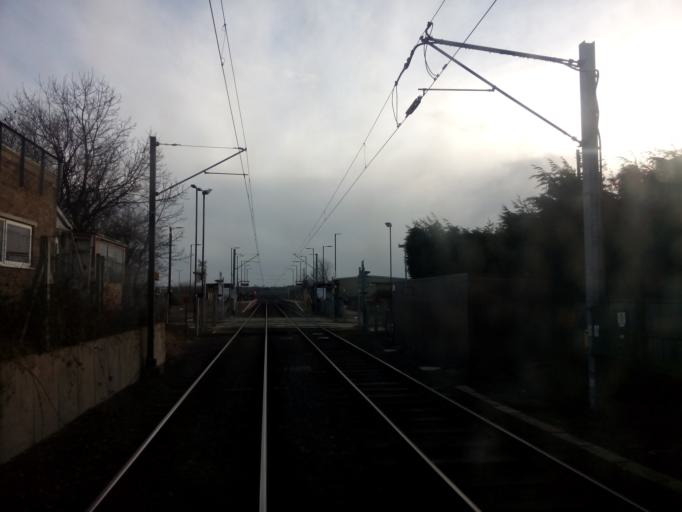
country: GB
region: England
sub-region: Newcastle upon Tyne
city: Dinnington
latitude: 55.0286
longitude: -1.7043
